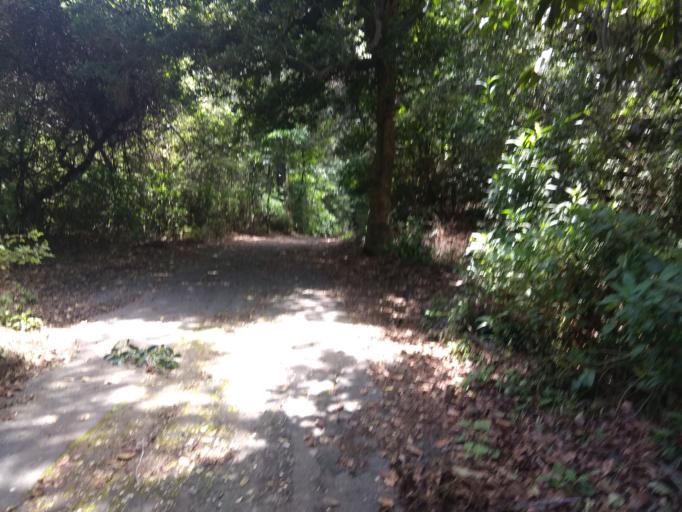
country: CR
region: Cartago
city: Cot
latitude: 9.9655
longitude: -83.8719
